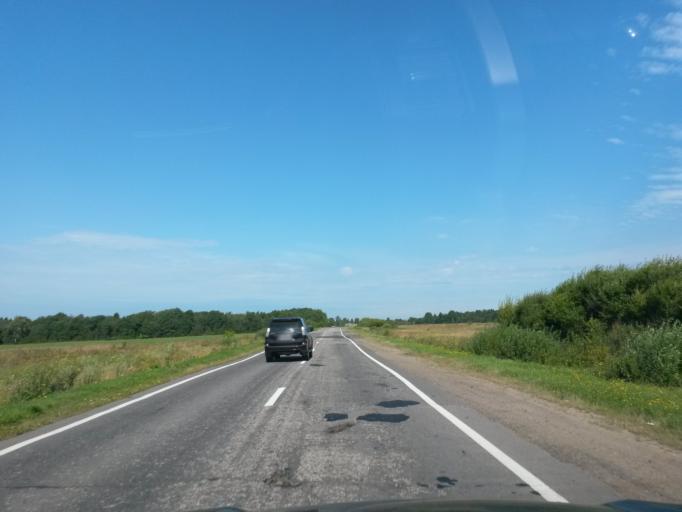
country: RU
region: Jaroslavl
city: Konstantinovskiy
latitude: 57.8355
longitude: 39.6607
